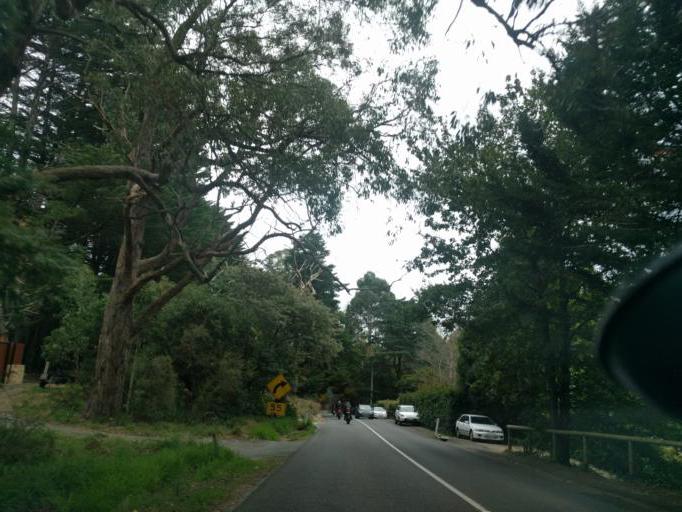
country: AU
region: South Australia
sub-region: Adelaide Hills
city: Stirling
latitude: -35.0166
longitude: 138.7408
